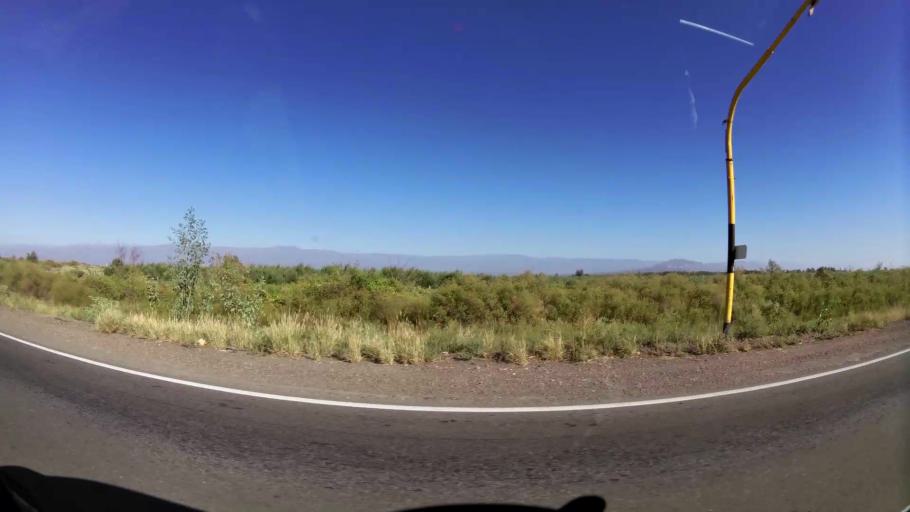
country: AR
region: Mendoza
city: General Lavalle
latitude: -32.7098
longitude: -68.6769
